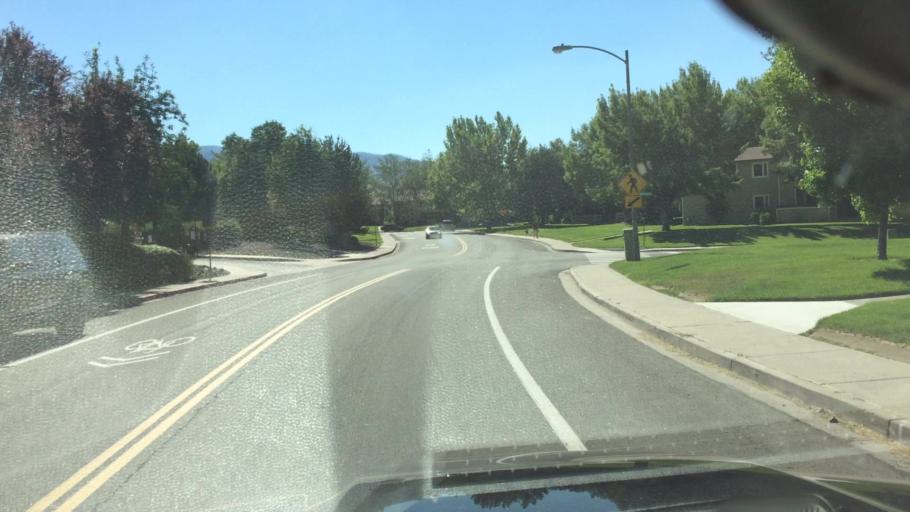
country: US
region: Nevada
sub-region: Washoe County
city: Sparks
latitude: 39.4536
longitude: -119.7726
